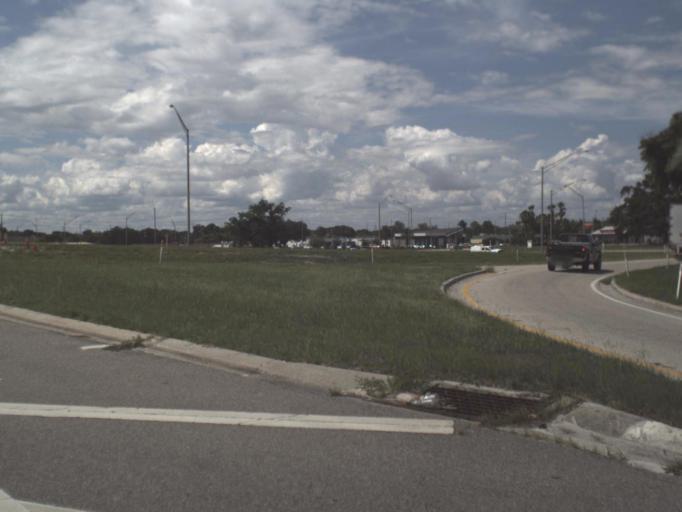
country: US
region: Florida
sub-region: Polk County
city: Lake Wales
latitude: 27.8974
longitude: -81.5981
